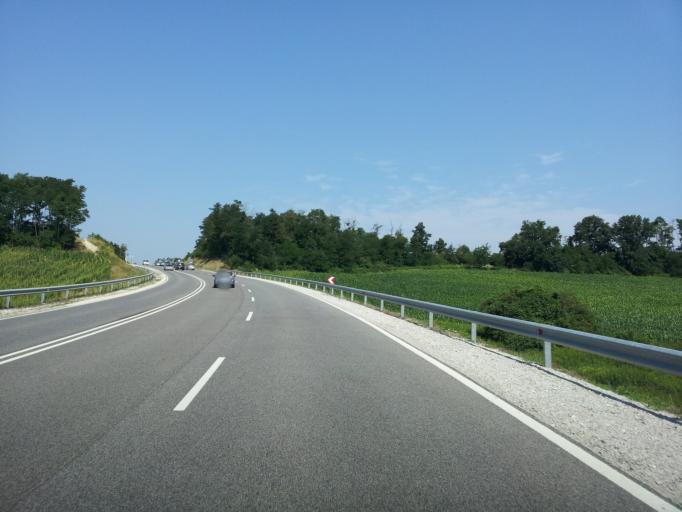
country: HU
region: Zala
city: Pacsa
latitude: 46.8286
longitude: 17.0523
